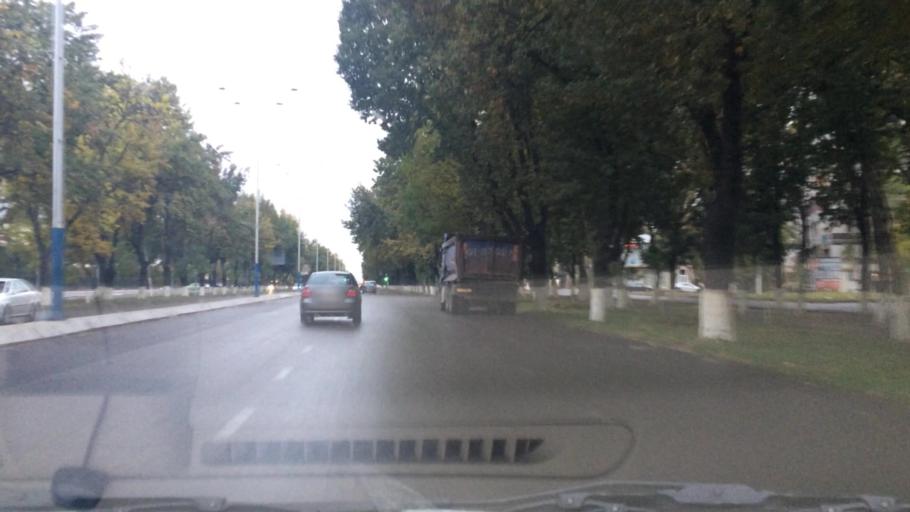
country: UZ
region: Toshkent Shahri
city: Tashkent
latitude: 41.2709
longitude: 69.2022
